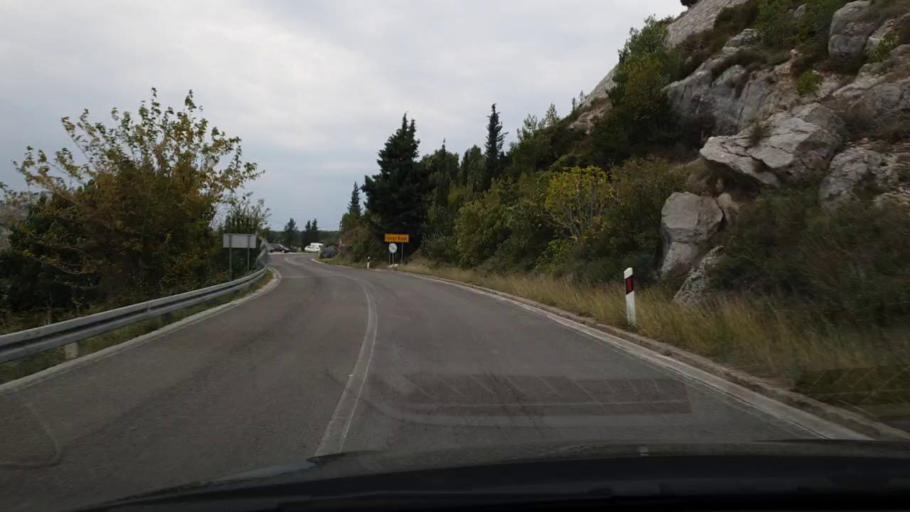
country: HR
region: Dubrovacko-Neretvanska
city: Cibaca
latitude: 42.6486
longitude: 18.1592
